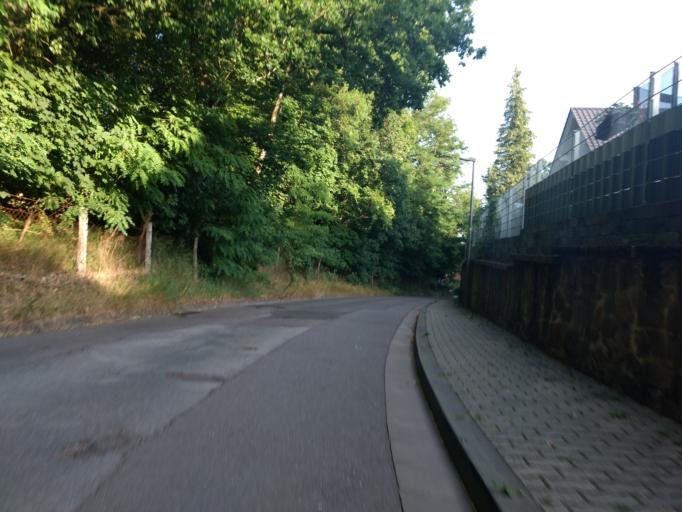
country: DE
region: Saarland
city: Wallerfangen
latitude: 49.3214
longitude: 6.7252
